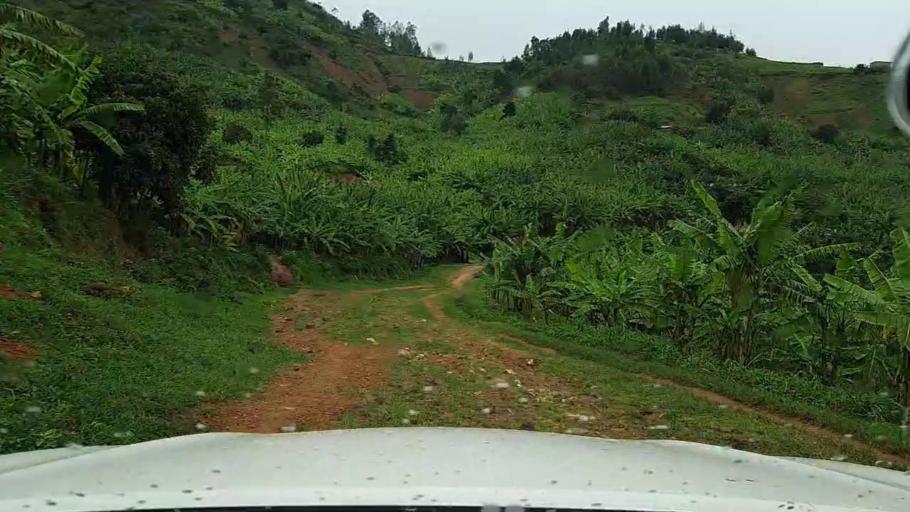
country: RW
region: Kigali
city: Kigali
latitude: -1.9009
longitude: 29.9545
